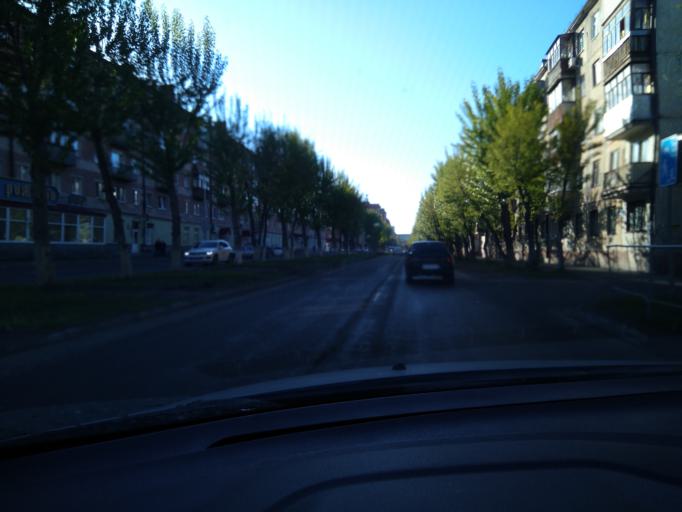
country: RU
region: Tjumen
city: Tyumen
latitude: 57.1315
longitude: 65.5875
